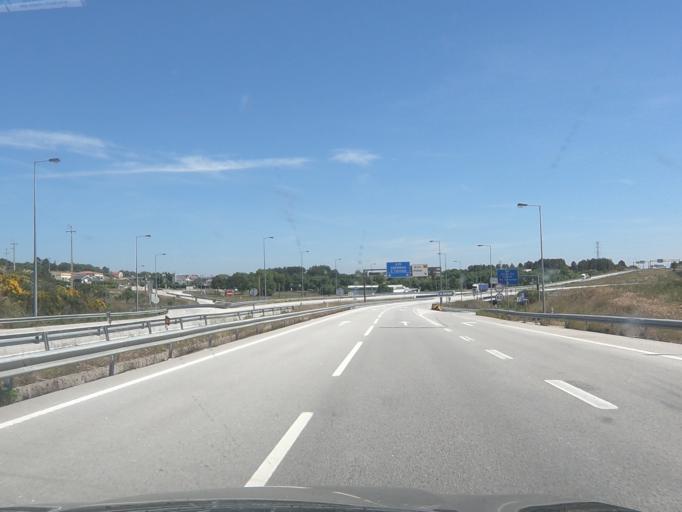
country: PT
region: Guarda
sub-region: Guarda
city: Sequeira
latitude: 40.5646
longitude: -7.2225
